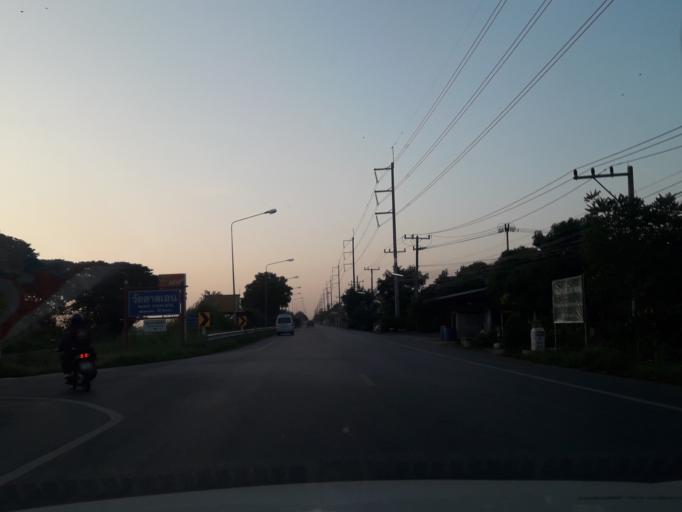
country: TH
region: Phra Nakhon Si Ayutthaya
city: Maha Rat
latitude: 14.5154
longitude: 100.5448
